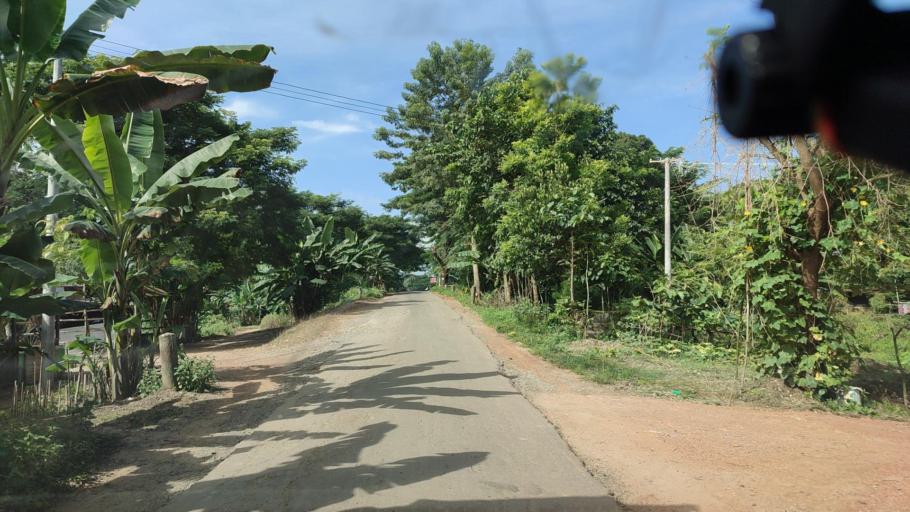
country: MM
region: Bago
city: Letpandan
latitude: 17.7445
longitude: 95.6300
